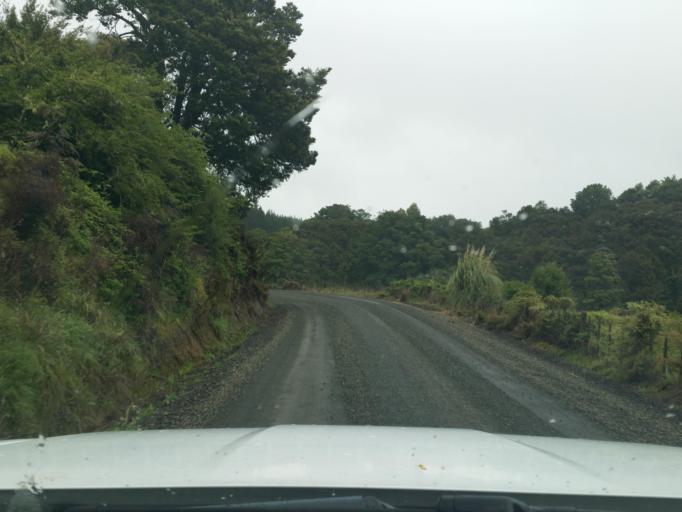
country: NZ
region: Northland
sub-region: Kaipara District
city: Dargaville
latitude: -35.8086
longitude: 173.9923
